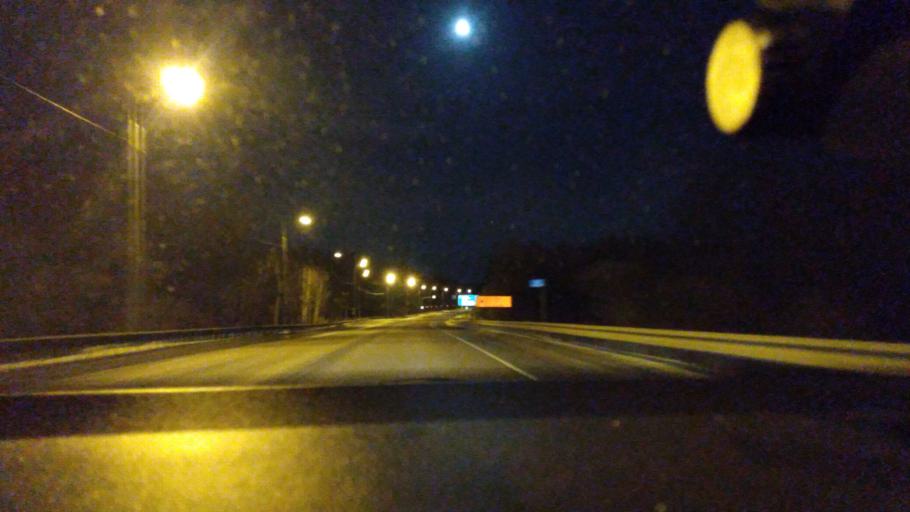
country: RU
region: Moskovskaya
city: Il'inskiy Pogost
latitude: 55.4871
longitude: 38.9129
